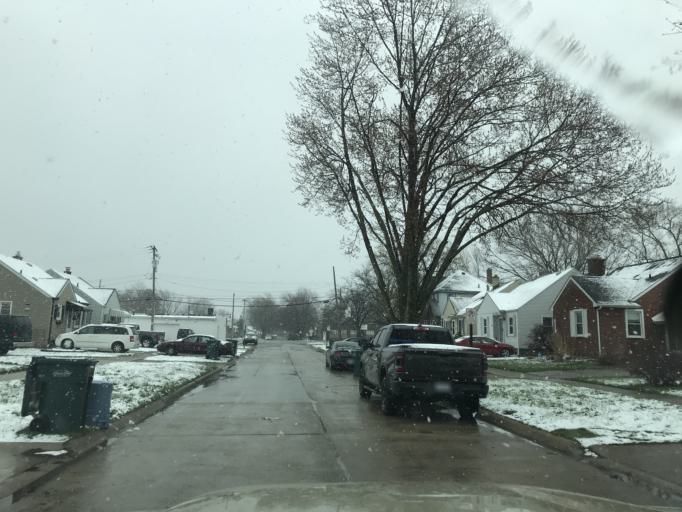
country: US
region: Michigan
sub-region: Wayne County
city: Lincoln Park
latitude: 42.2621
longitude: -83.1894
